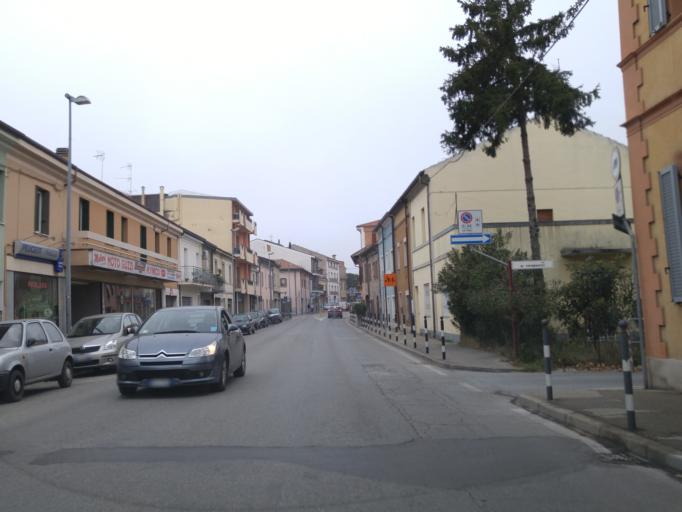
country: IT
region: Emilia-Romagna
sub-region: Provincia di Rimini
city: Cattolica
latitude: 43.9616
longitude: 12.7457
